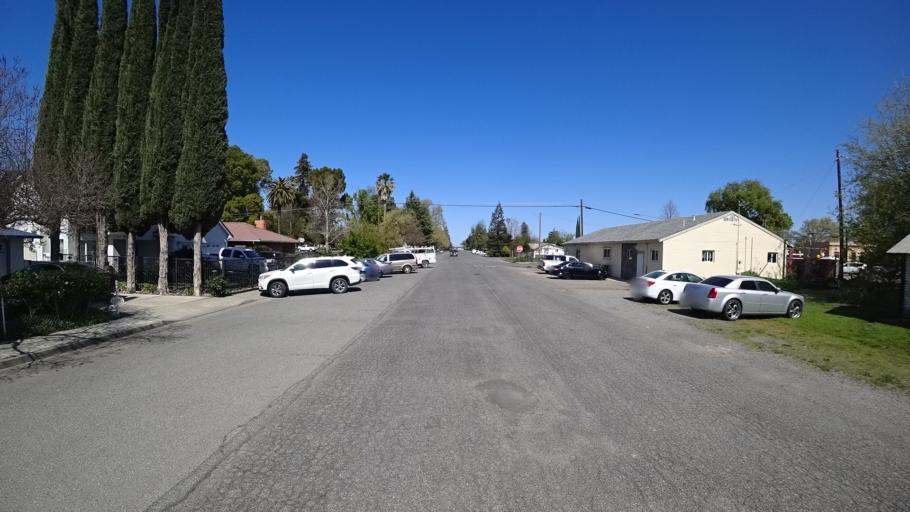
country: US
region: California
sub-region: Glenn County
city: Hamilton City
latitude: 39.7392
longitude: -122.0124
